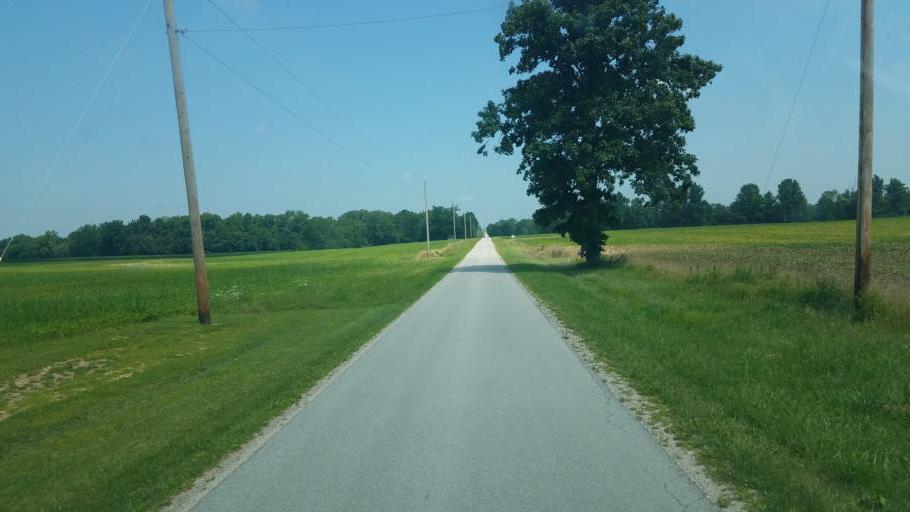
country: US
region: Ohio
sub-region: Sandusky County
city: Green Springs
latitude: 41.0705
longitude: -82.9769
